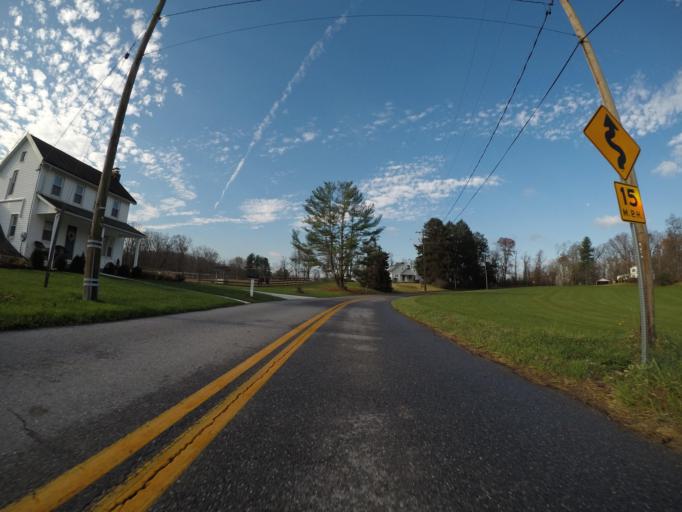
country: US
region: Maryland
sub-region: Carroll County
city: Hampstead
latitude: 39.5730
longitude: -76.8165
